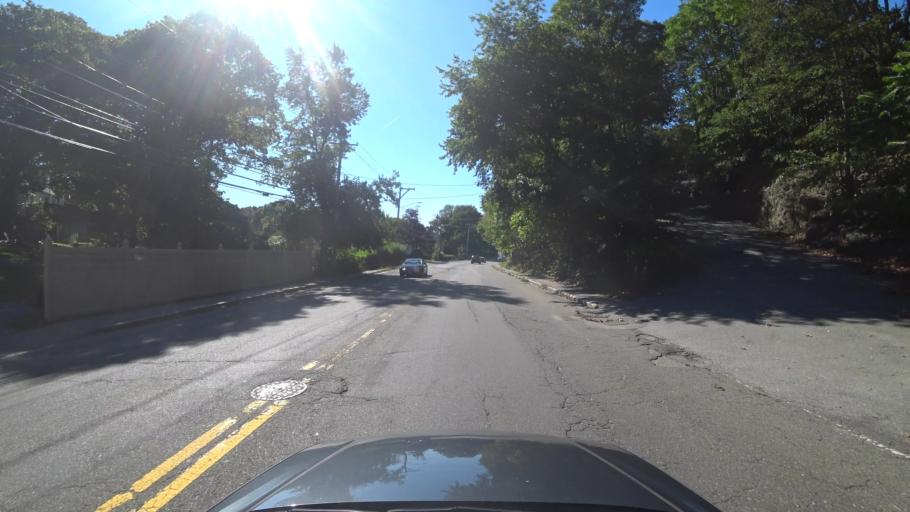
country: US
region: Massachusetts
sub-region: Essex County
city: Swampscott
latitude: 42.4767
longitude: -70.9110
